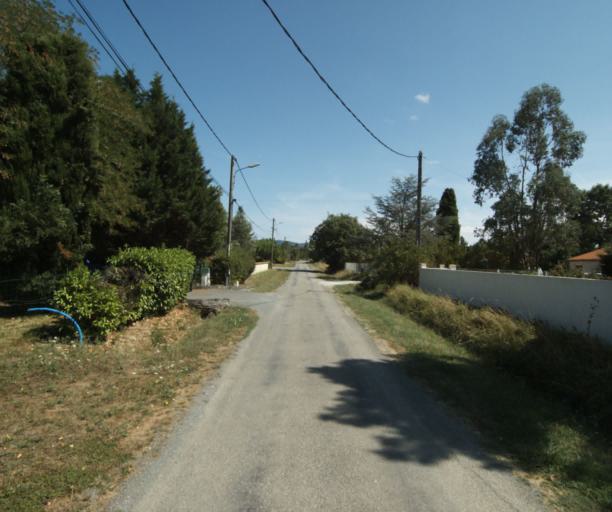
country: FR
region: Midi-Pyrenees
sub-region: Departement de la Haute-Garonne
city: Revel
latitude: 43.4843
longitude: 2.0042
